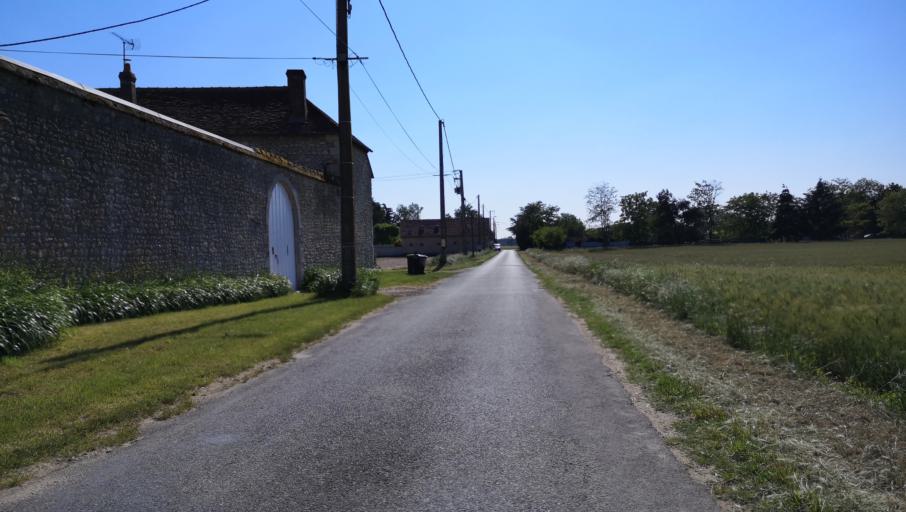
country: FR
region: Centre
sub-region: Departement du Loiret
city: Mareau-aux-Pres
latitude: 47.8604
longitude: 1.7866
